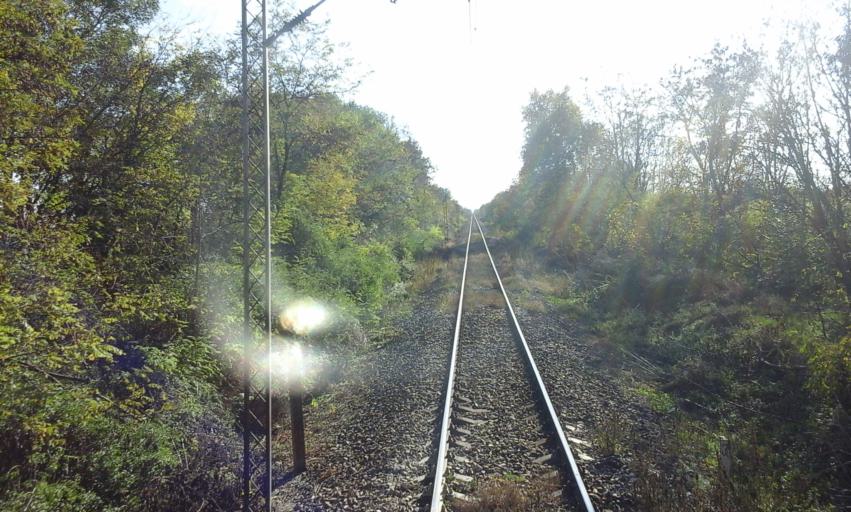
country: RS
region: Autonomna Pokrajina Vojvodina
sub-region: Severnobacki Okrug
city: Backa Topola
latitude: 45.8458
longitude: 19.6538
